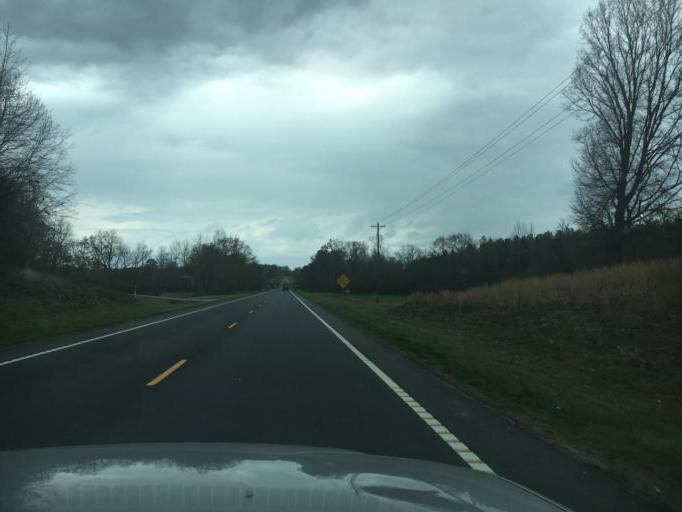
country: US
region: South Carolina
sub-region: Oconee County
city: Walhalla
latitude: 34.7892
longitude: -83.0219
